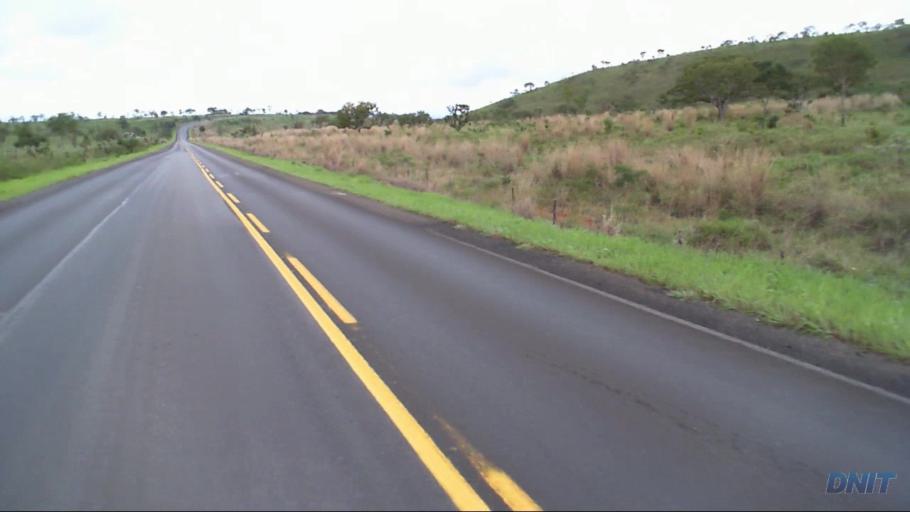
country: BR
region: Goias
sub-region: Padre Bernardo
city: Padre Bernardo
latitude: -15.2077
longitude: -48.4676
